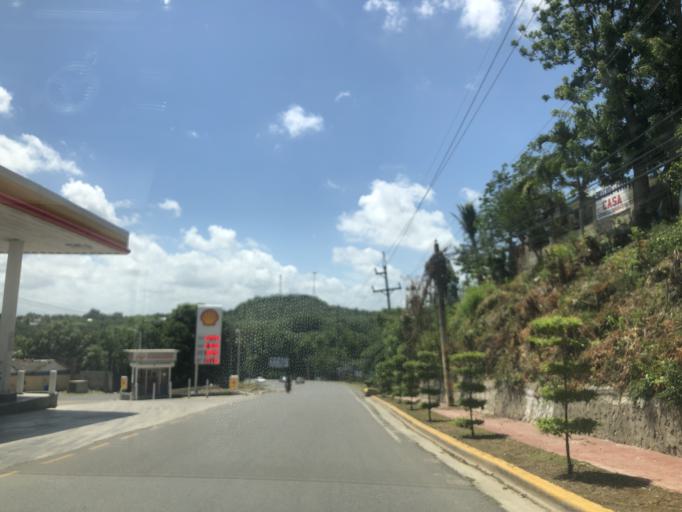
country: DO
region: Santiago
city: La Canela
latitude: 19.4515
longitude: -70.7676
